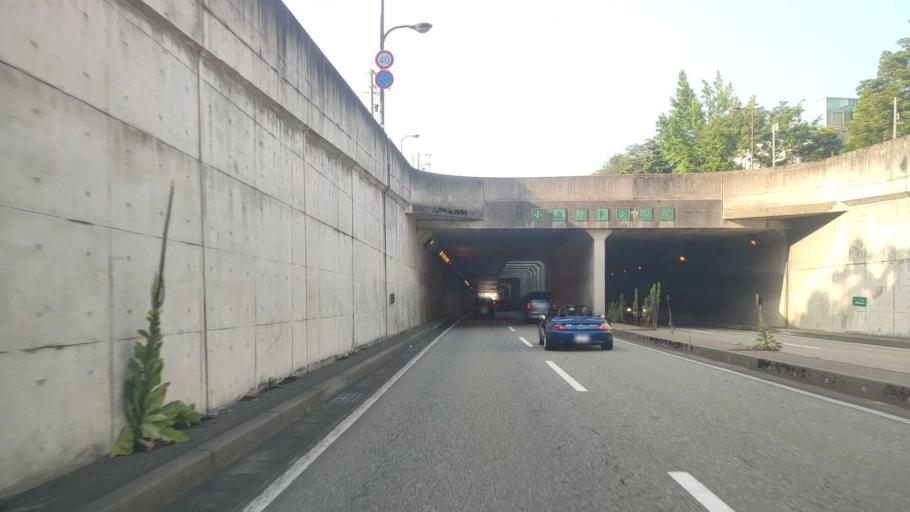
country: JP
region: Ishikawa
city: Nonoichi
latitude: 36.5553
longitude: 136.6758
